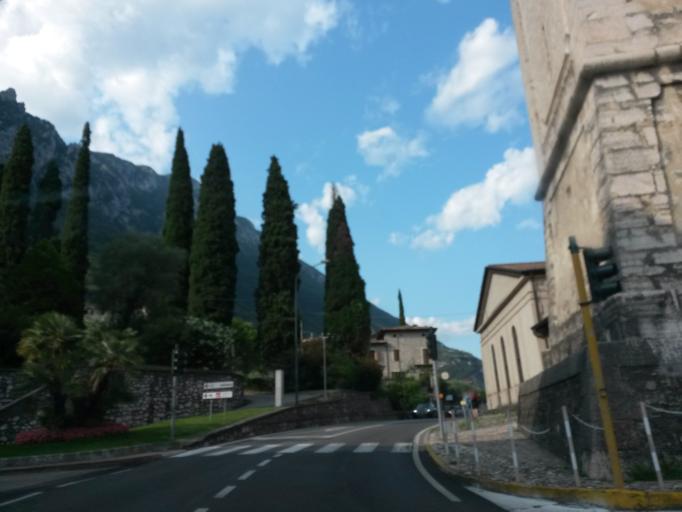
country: IT
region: Lombardy
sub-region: Provincia di Brescia
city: Gargnano
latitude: 45.6906
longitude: 10.6644
